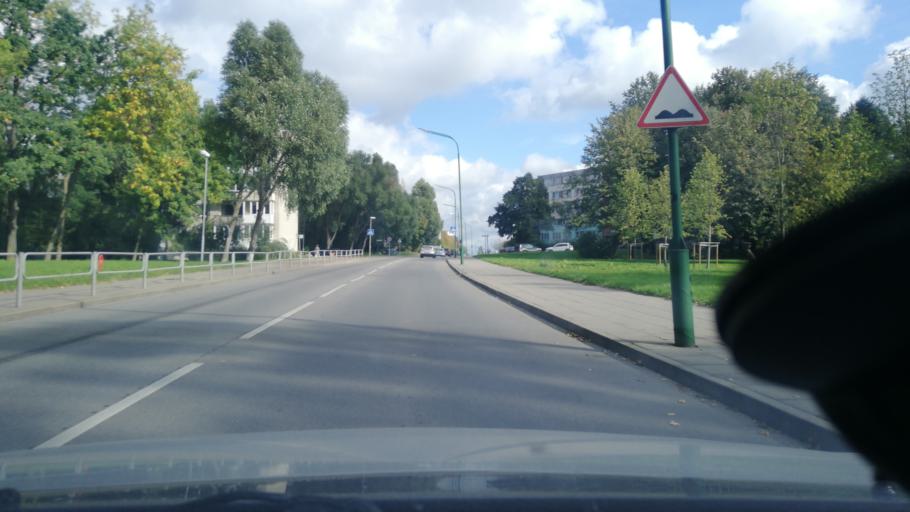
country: LT
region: Klaipedos apskritis
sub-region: Klaipeda
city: Klaipeda
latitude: 55.6838
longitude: 21.1761
